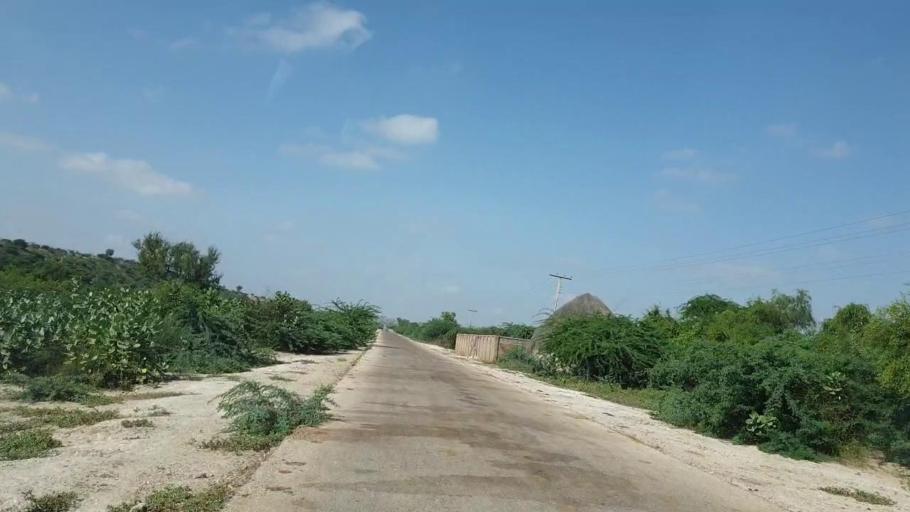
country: PK
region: Sindh
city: Mithi
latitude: 24.5310
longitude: 69.8394
